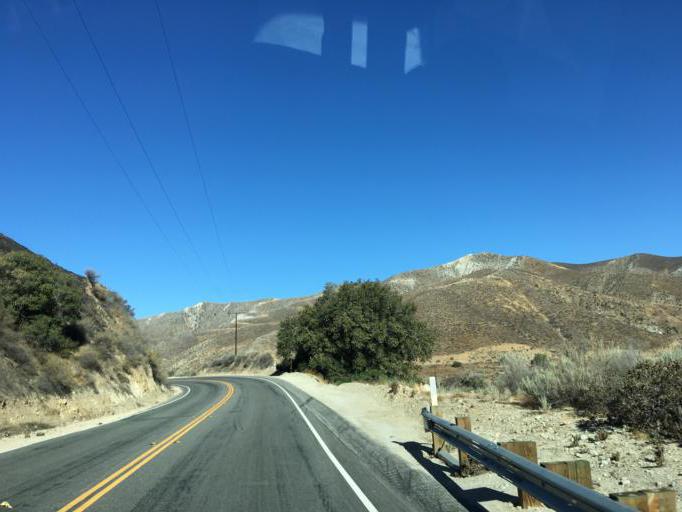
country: US
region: California
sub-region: Los Angeles County
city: Agua Dulce
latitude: 34.4373
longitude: -118.3303
